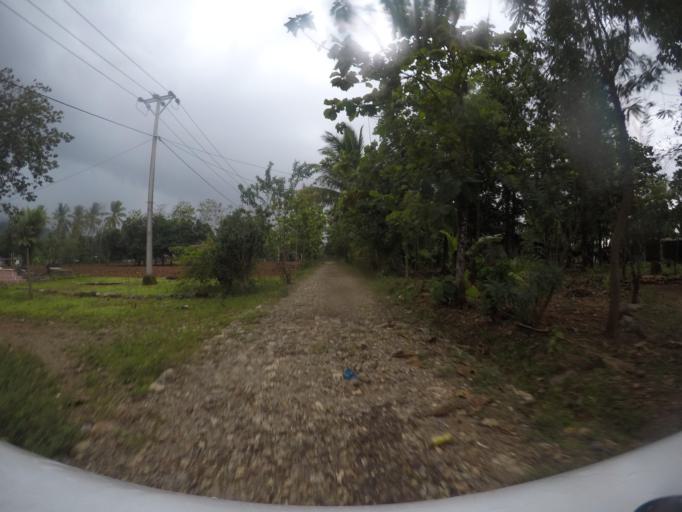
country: TL
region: Bobonaro
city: Maliana
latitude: -8.9620
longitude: 125.2144
